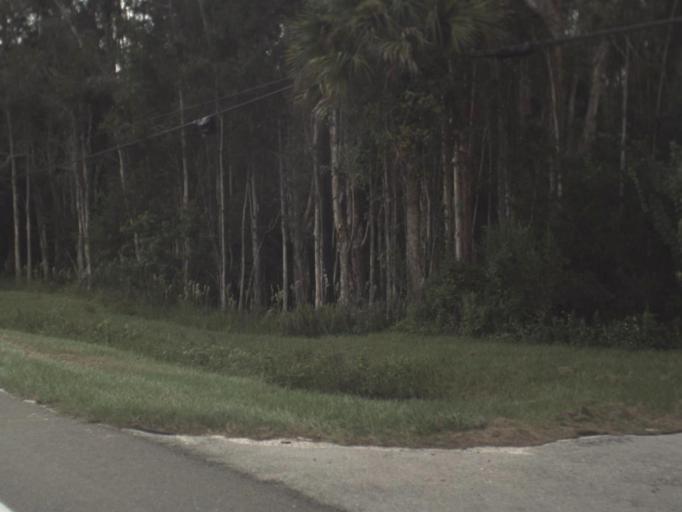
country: US
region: Florida
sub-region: Lee County
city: Fort Myers Shores
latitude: 26.7836
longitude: -81.7606
